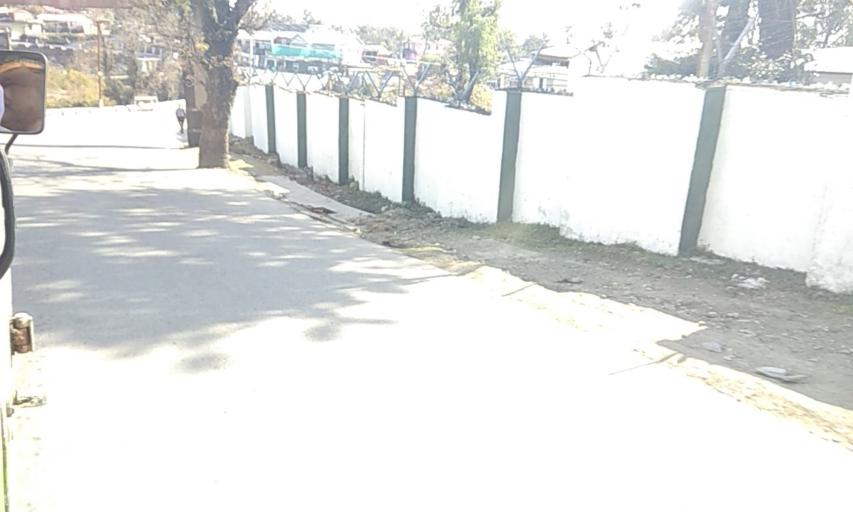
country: IN
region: Himachal Pradesh
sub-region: Kangra
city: Dharmsala
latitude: 32.1731
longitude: 76.3857
